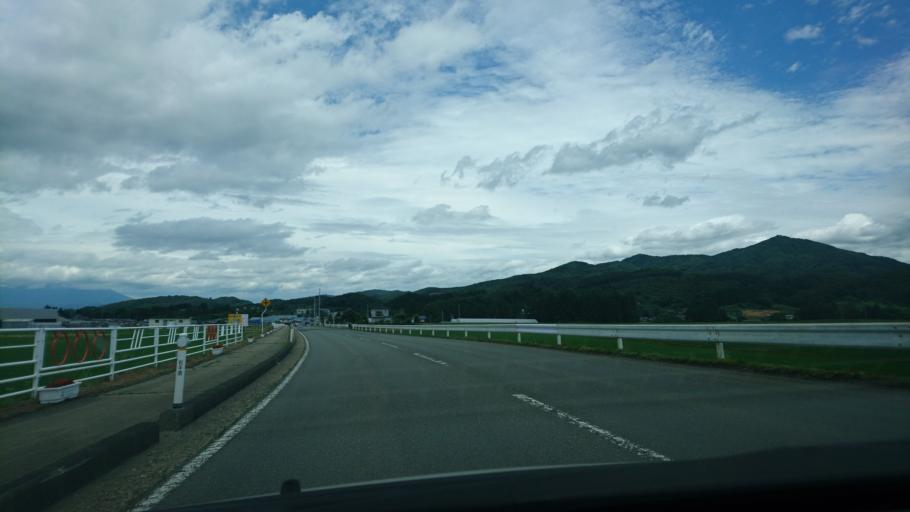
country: JP
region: Iwate
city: Morioka-shi
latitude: 39.6030
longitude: 141.2048
